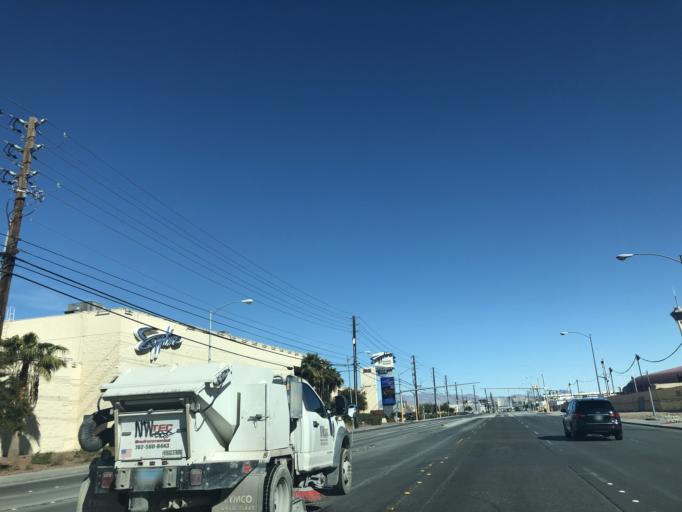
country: US
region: Nevada
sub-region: Clark County
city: Paradise
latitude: 36.1340
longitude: -115.1714
